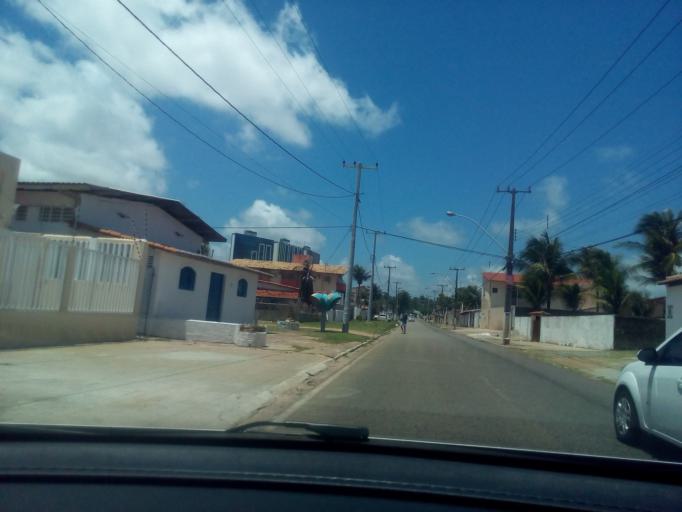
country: BR
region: Rio Grande do Norte
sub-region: Parnamirim
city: Parnamirim
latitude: -5.9618
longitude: -35.1477
